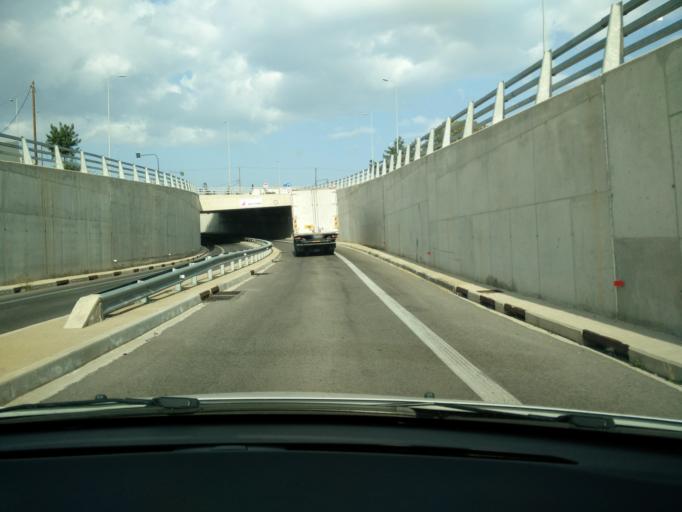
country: GR
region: Crete
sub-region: Nomos Lasithiou
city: Agios Nikolaos
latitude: 35.1839
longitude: 25.7048
